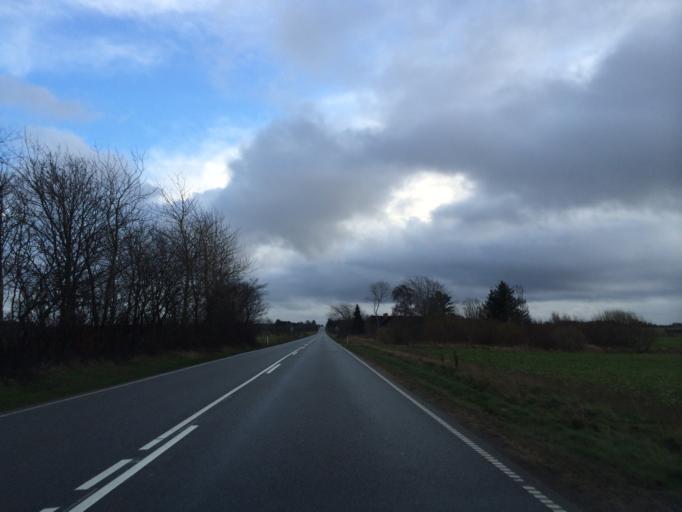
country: DK
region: Central Jutland
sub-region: Ringkobing-Skjern Kommune
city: Ringkobing
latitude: 56.0799
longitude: 8.3587
